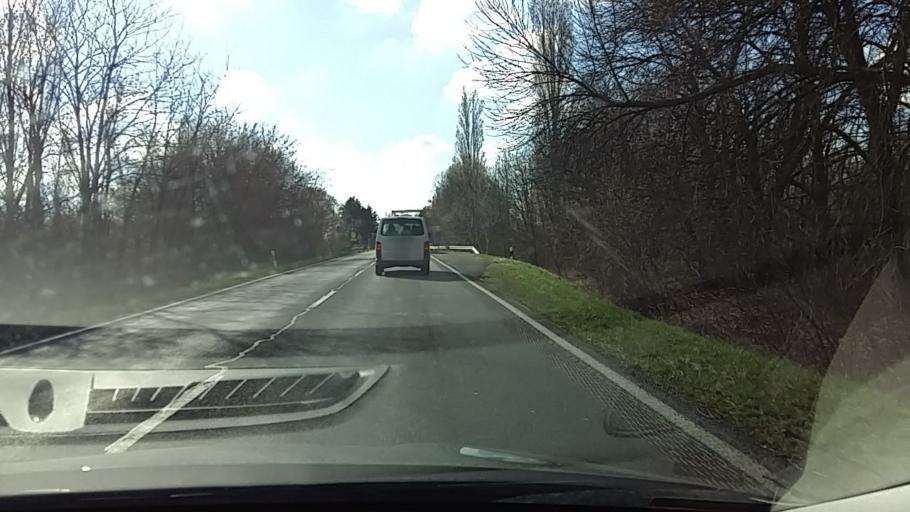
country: HU
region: Veszprem
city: Tapolca
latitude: 46.8373
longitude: 17.3727
